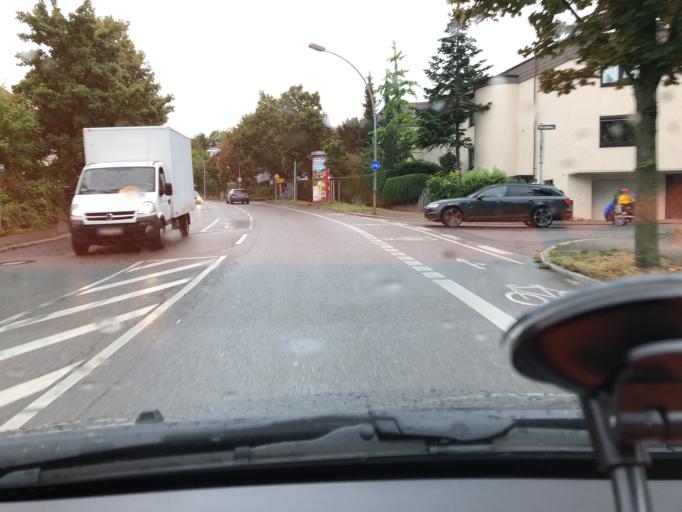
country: DE
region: Baden-Wuerttemberg
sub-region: Regierungsbezirk Stuttgart
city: Stuttgart-Ost
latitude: 48.7737
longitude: 9.1989
